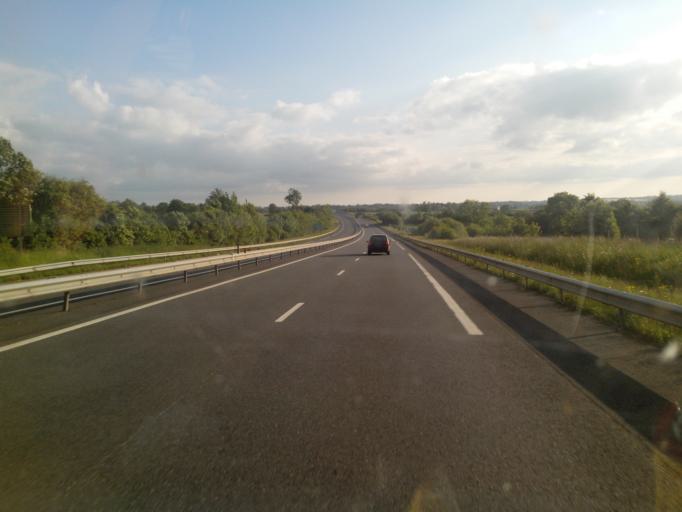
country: FR
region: Lower Normandy
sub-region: Departement du Calvados
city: Saint-Martin-des-Besaces
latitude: 49.0336
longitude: -0.8202
